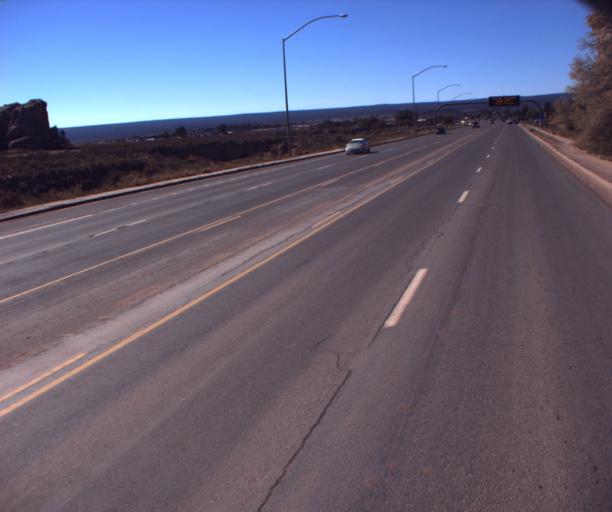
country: US
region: Arizona
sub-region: Apache County
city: Window Rock
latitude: 35.6631
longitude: -109.0492
